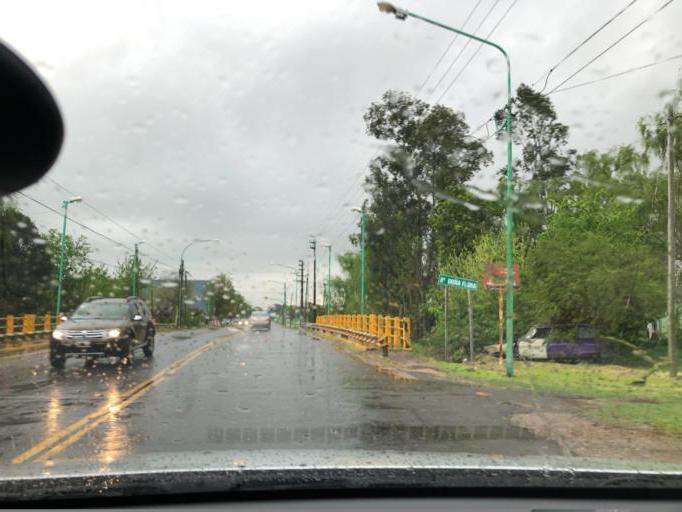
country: AR
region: Buenos Aires
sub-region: Partido de Ensenada
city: Ensenada
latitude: -34.8506
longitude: -57.9249
